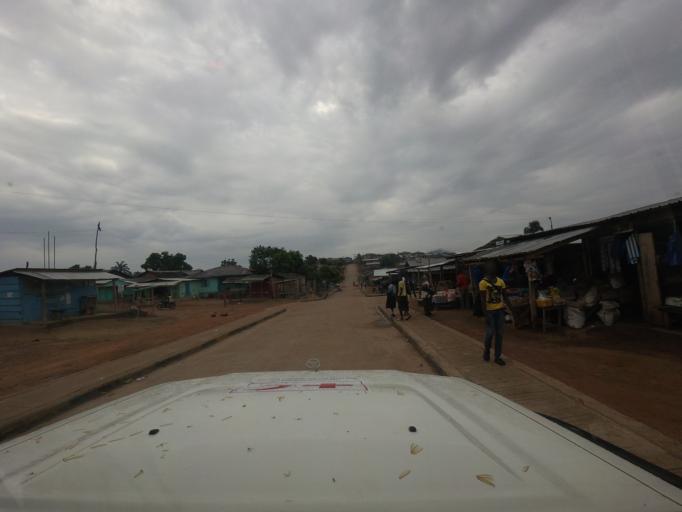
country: LR
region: Lofa
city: Voinjama
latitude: 8.4241
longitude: -9.7541
